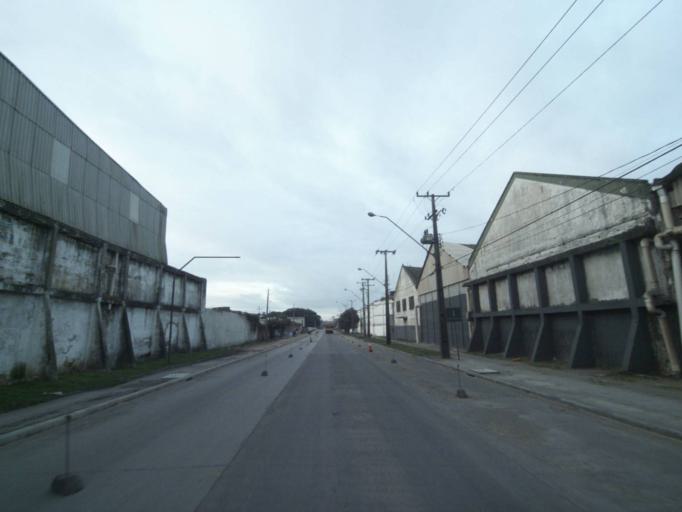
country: BR
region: Parana
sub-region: Paranagua
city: Paranagua
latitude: -25.5096
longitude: -48.5304
